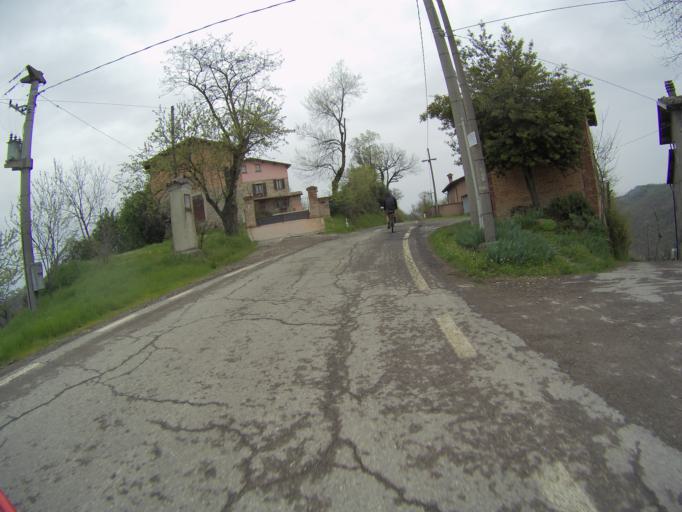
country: IT
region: Emilia-Romagna
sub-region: Provincia di Reggio Emilia
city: San Polo d'Enza
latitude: 44.6091
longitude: 10.4489
